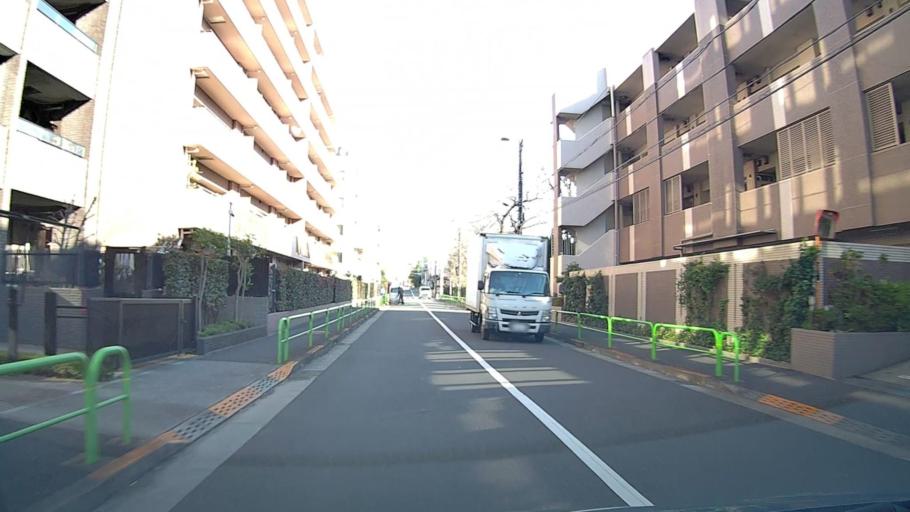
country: JP
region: Tokyo
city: Tokyo
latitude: 35.7287
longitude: 139.6450
